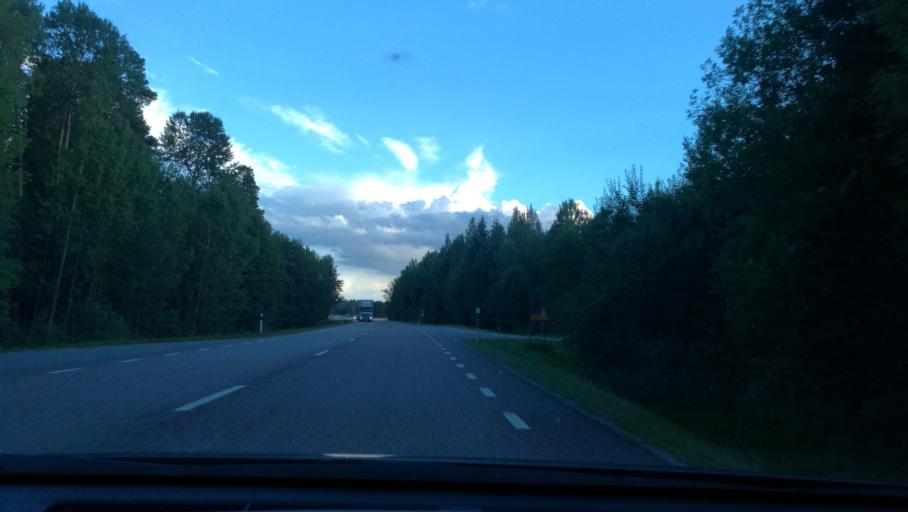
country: SE
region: Soedermanland
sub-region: Katrineholms Kommun
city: Katrineholm
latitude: 59.0271
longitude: 16.2138
